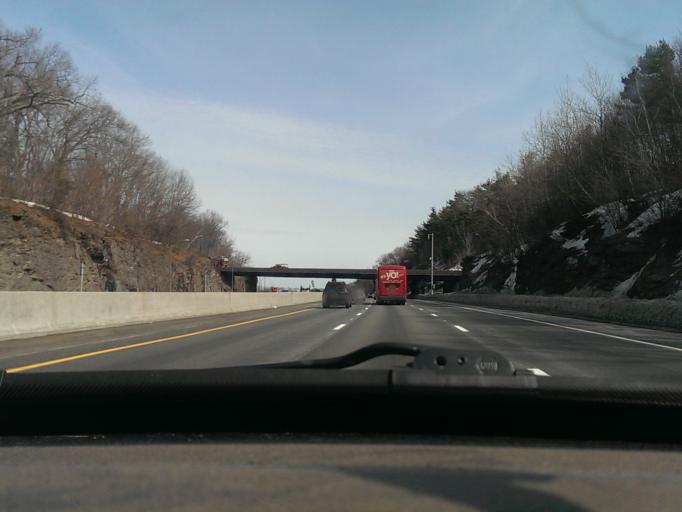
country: US
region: Massachusetts
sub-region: Worcester County
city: Auburn
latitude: 42.1918
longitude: -71.8552
